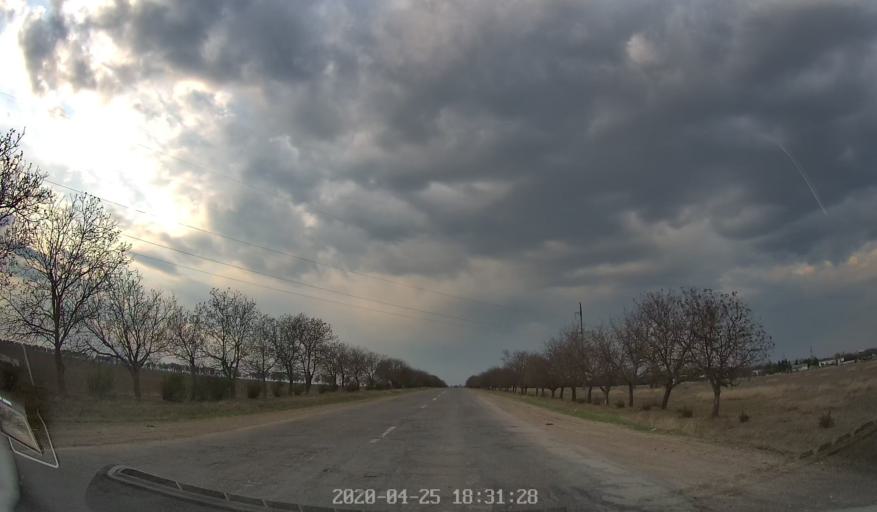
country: MD
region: Criuleni
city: Criuleni
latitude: 47.2178
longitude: 29.1471
